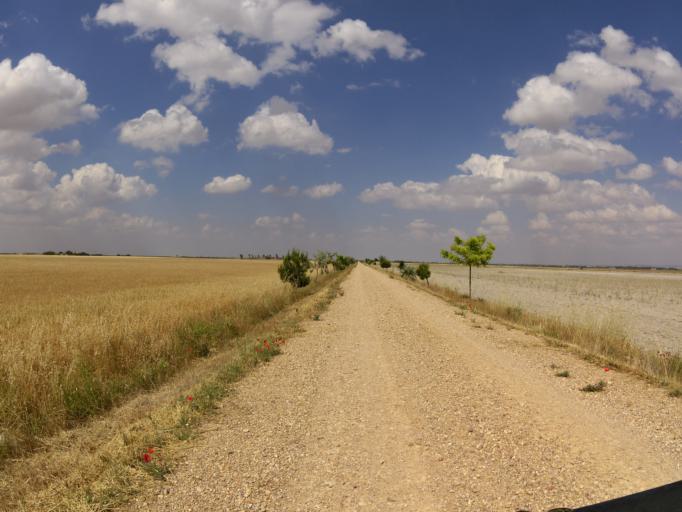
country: ES
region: Castille-La Mancha
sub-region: Provincia de Albacete
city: Albacete
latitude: 38.9348
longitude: -1.9888
